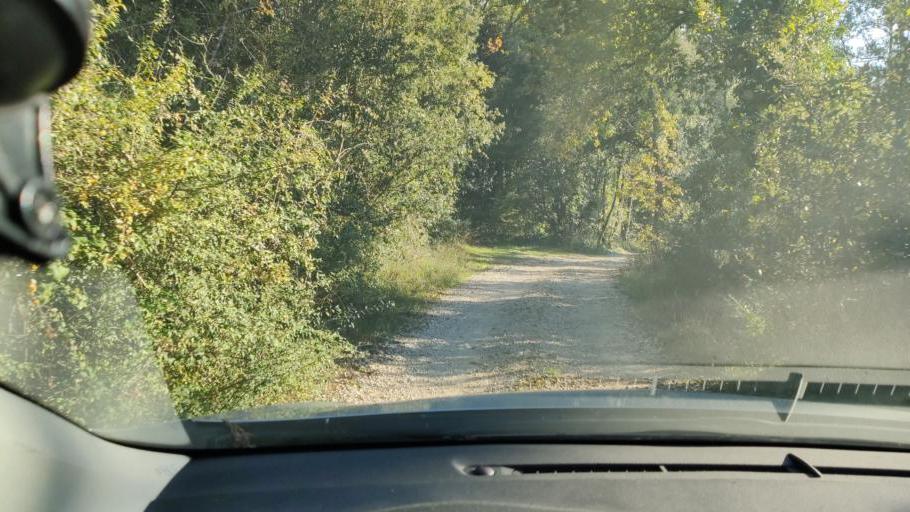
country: IT
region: Umbria
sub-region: Provincia di Terni
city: Amelia
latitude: 42.5791
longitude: 12.4358
